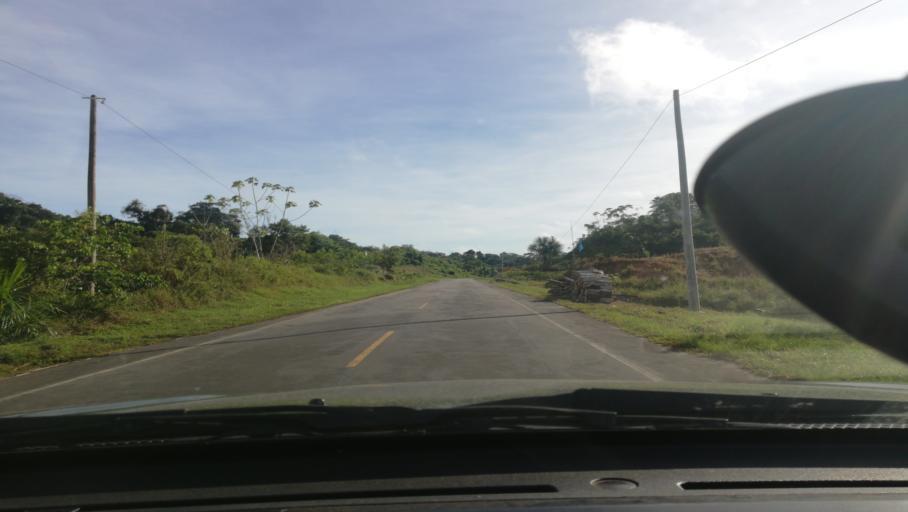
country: PE
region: Loreto
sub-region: Provincia de Loreto
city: Nauta
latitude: -4.3663
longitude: -73.5592
